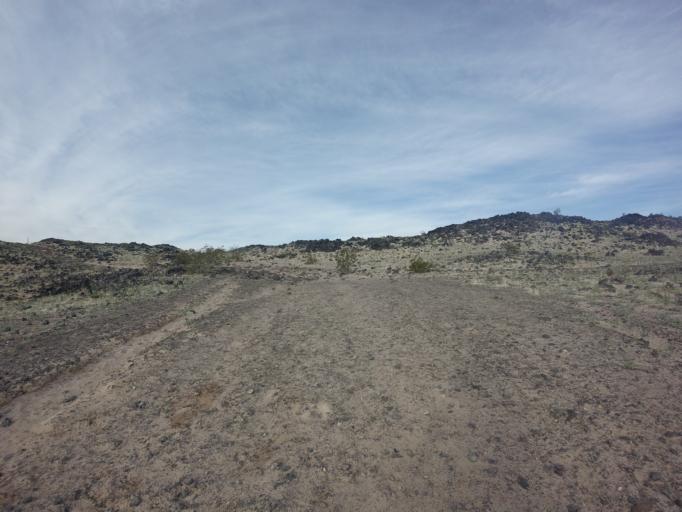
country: US
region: California
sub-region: San Bernardino County
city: Twentynine Palms
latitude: 34.5478
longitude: -115.7913
